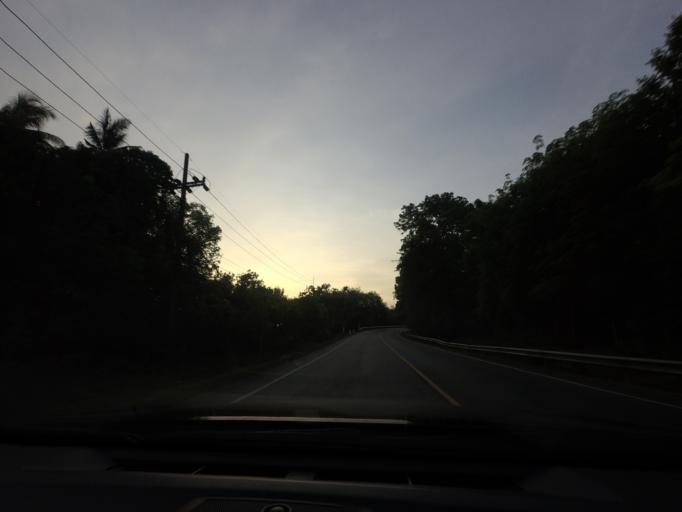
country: TH
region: Narathiwat
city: Rueso
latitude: 6.3597
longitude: 101.6115
